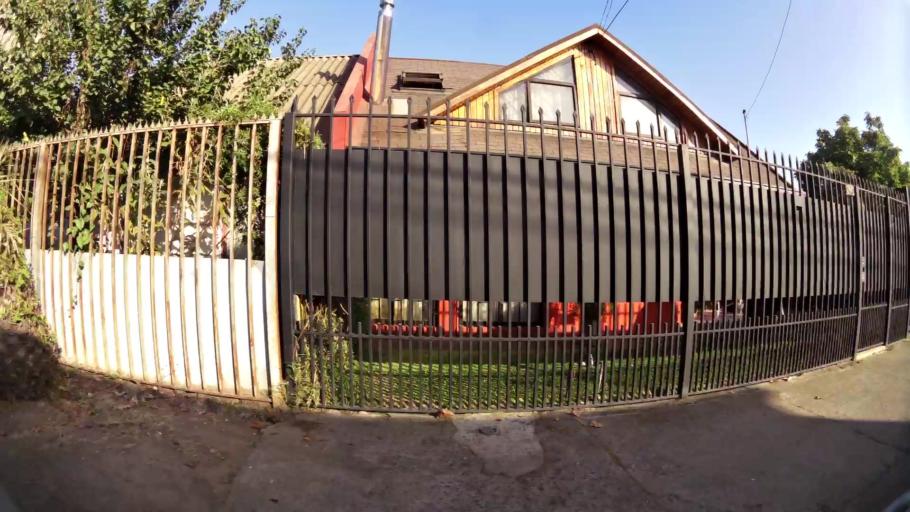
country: CL
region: Maule
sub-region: Provincia de Talca
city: Talca
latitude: -35.4117
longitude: -71.6531
